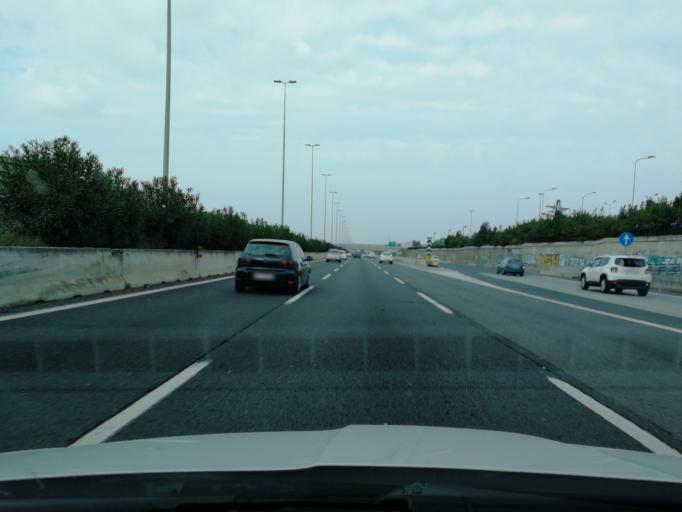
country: IT
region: Latium
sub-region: Citta metropolitana di Roma Capitale
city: Ciampino
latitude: 41.8491
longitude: 12.5963
